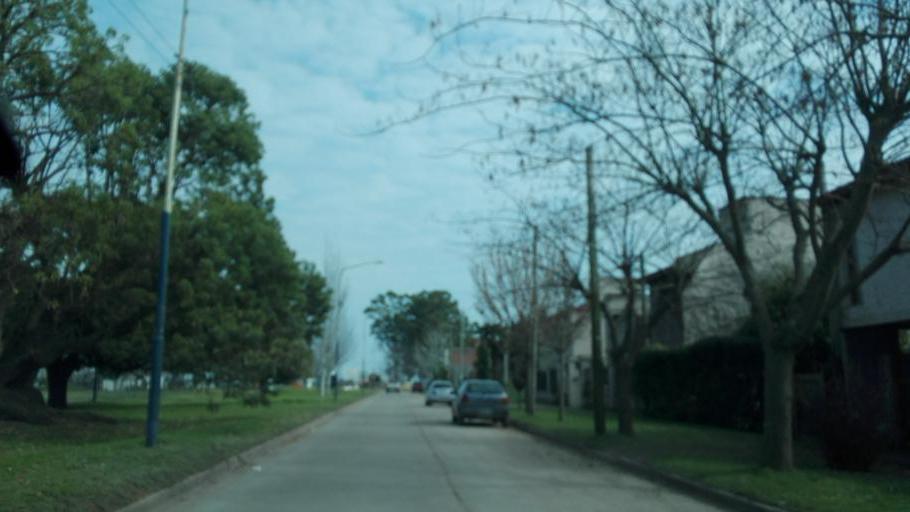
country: AR
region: Buenos Aires
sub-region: Partido de Chascomus
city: Chascomus
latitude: -35.5690
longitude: -58.0232
